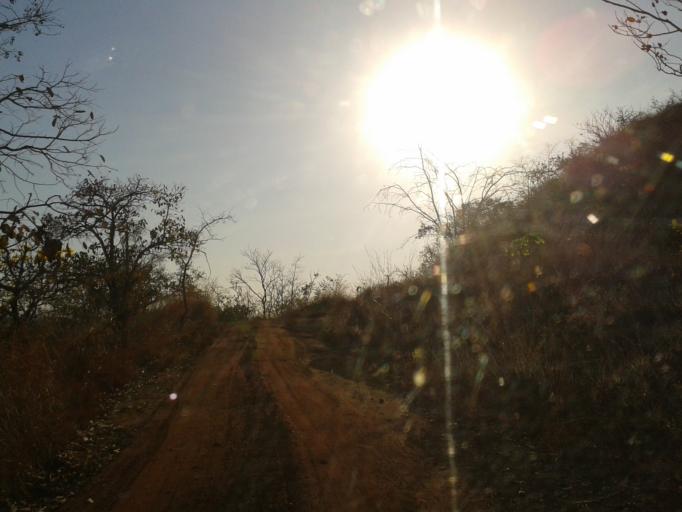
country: BR
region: Minas Gerais
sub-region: Santa Vitoria
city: Santa Vitoria
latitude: -19.1862
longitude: -50.0305
